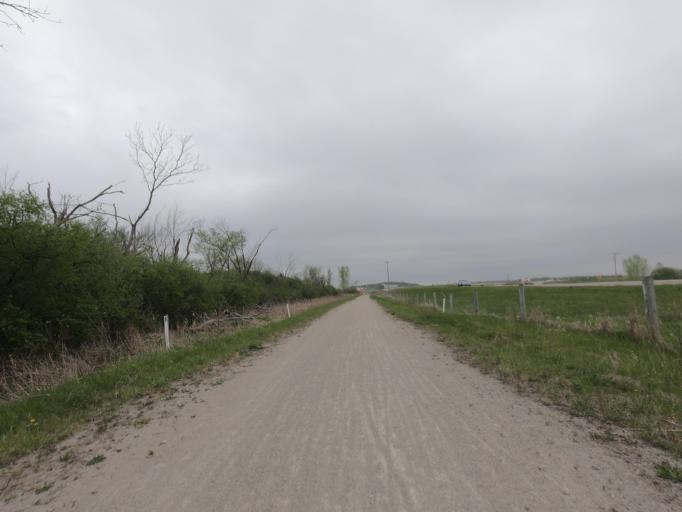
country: US
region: Wisconsin
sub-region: Jefferson County
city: Jefferson
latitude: 43.0380
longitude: -88.8033
